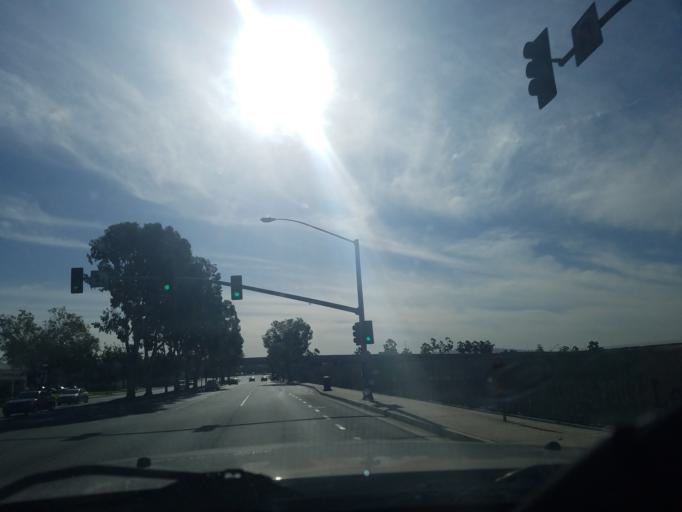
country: US
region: California
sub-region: Orange County
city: Irvine
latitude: 33.7075
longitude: -117.8078
